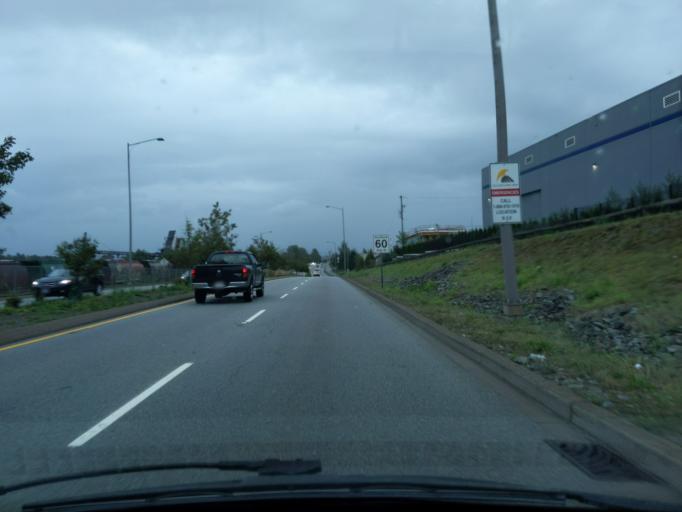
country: CA
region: British Columbia
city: Pitt Meadows
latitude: 49.1805
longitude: -122.7092
